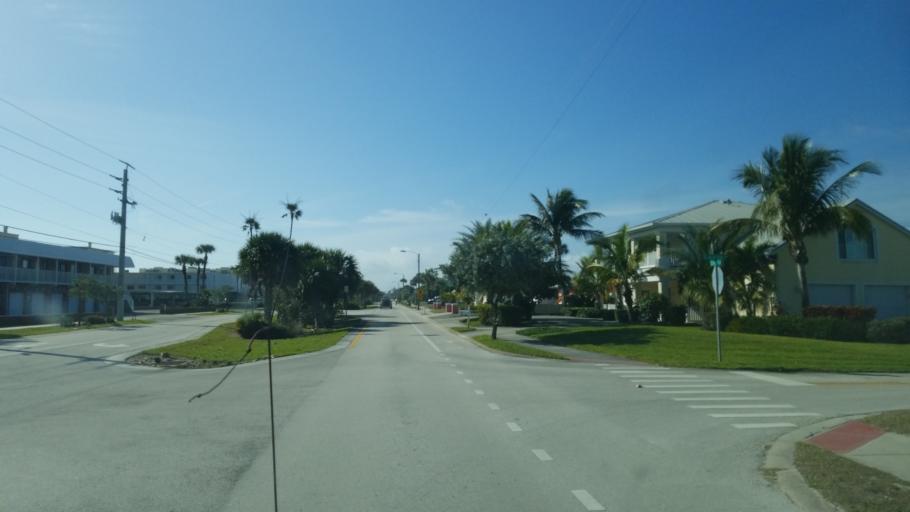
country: US
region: Florida
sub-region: Brevard County
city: Cape Canaveral
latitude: 28.3651
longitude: -80.6045
